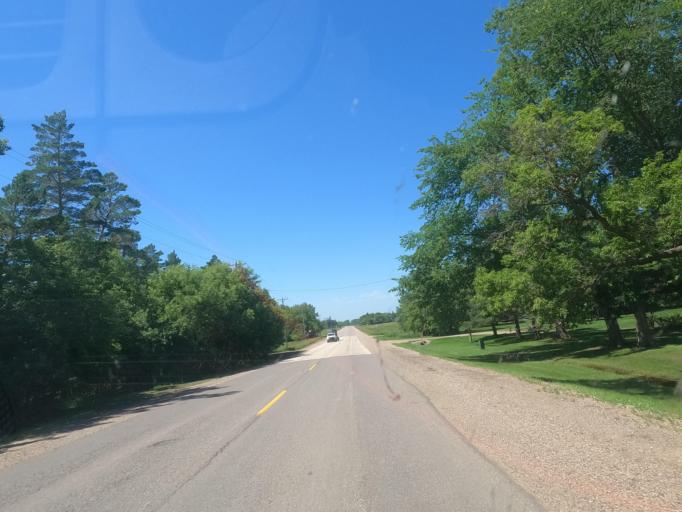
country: CA
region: Manitoba
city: Souris
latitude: 49.6211
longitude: -100.2738
